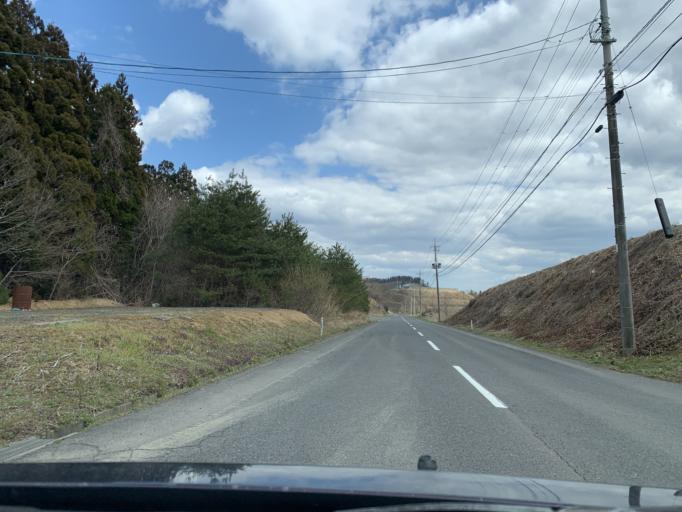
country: JP
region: Iwate
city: Ichinoseki
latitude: 38.8254
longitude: 141.2931
